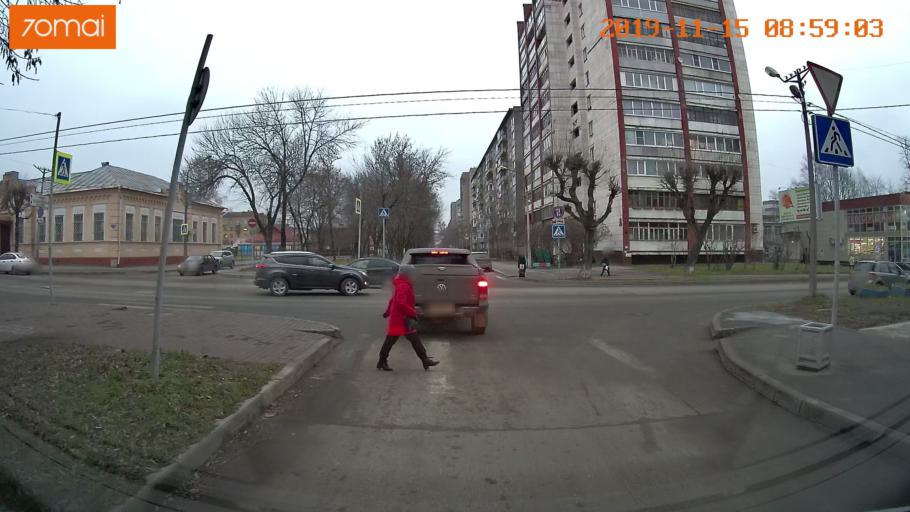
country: RU
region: Vologda
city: Cherepovets
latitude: 59.1282
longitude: 37.9240
